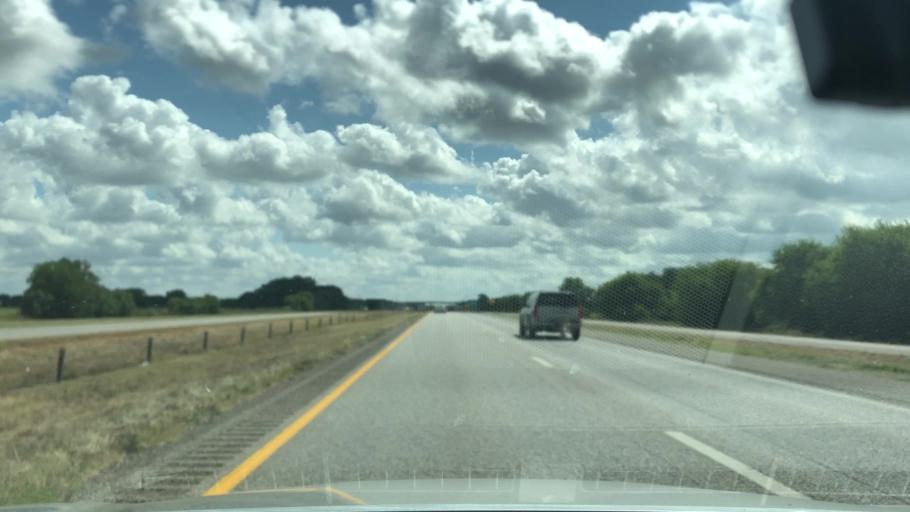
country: US
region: Texas
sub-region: Guadalupe County
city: Cibolo
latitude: 29.5047
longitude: -98.1768
